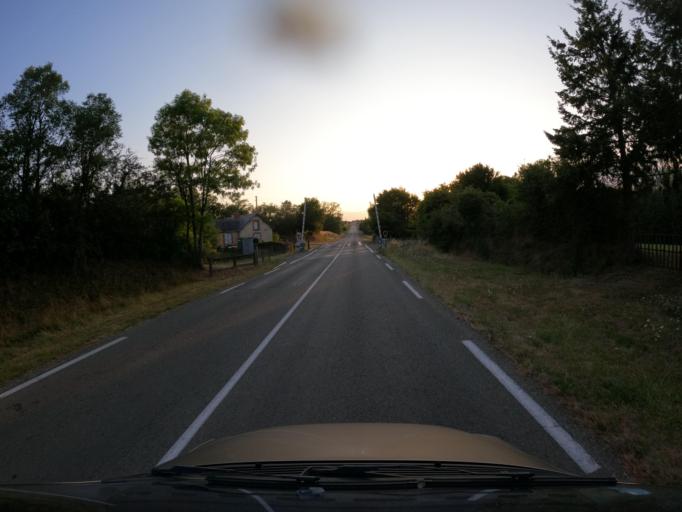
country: FR
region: Pays de la Loire
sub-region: Departement de la Mayenne
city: Meslay-du-Maine
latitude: 47.8732
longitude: -0.5116
